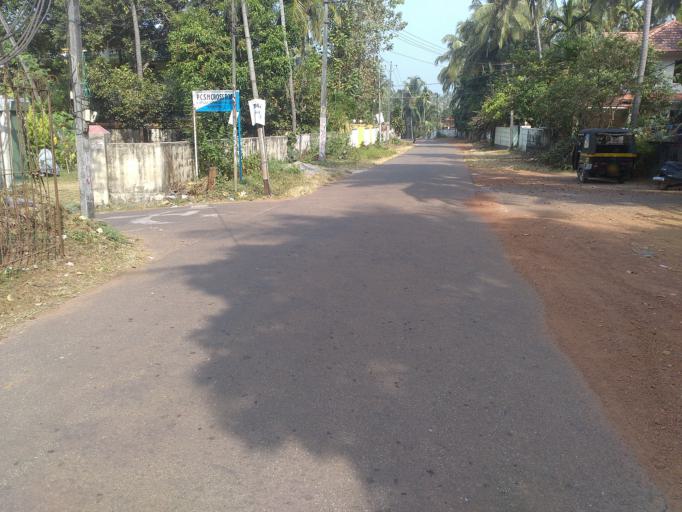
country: IN
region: Kerala
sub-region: Kozhikode
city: Kozhikode
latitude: 11.2963
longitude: 75.8169
